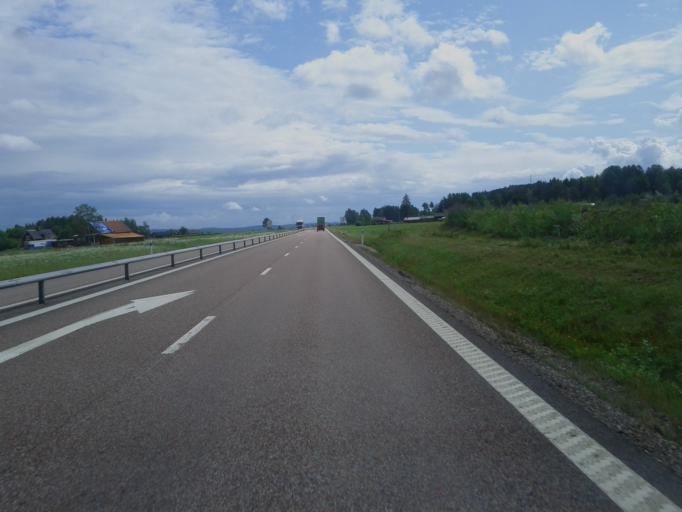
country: SE
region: Dalarna
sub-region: Hedemora Kommun
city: Hedemora
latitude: 60.3074
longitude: 15.9528
